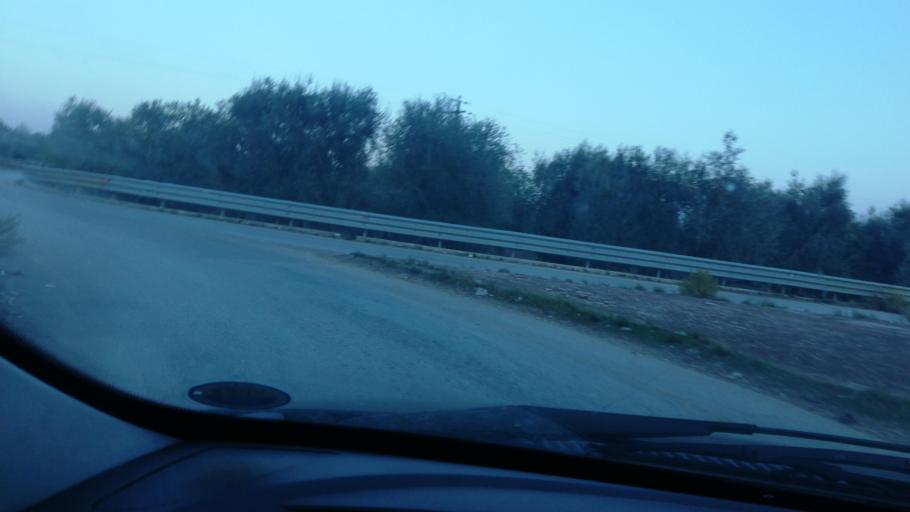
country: IT
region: Apulia
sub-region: Provincia di Bari
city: Bitonto
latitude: 41.1282
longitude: 16.7127
